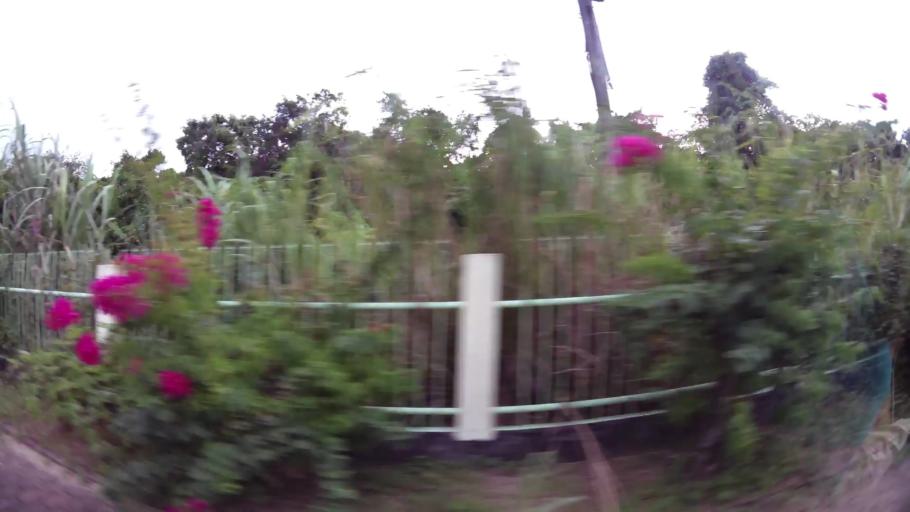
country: SR
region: Paramaribo
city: Paramaribo
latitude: 5.8603
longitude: -55.1770
